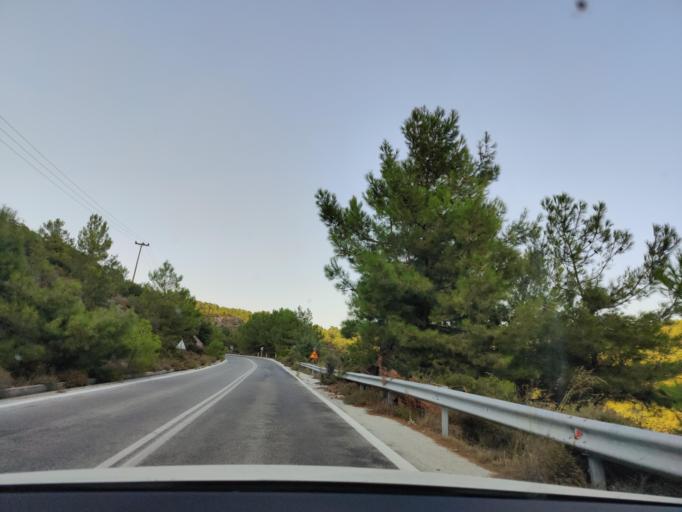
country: GR
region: East Macedonia and Thrace
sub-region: Nomos Kavalas
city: Potamia
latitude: 40.6219
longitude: 24.7613
